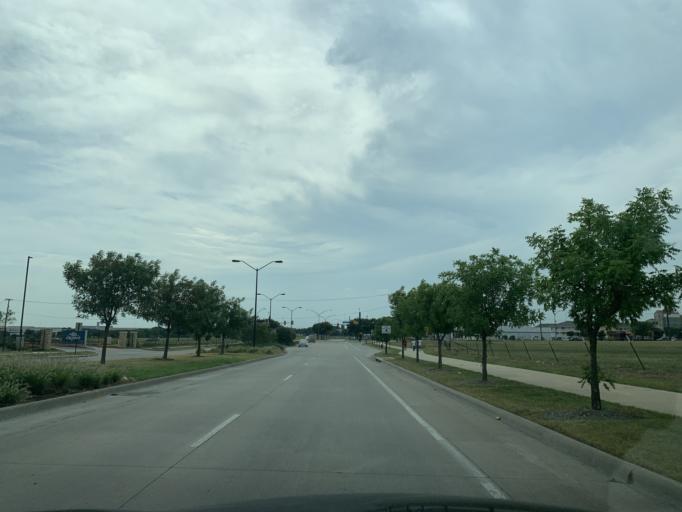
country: US
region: Texas
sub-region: Tarrant County
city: Haltom City
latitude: 32.8349
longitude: -97.2884
